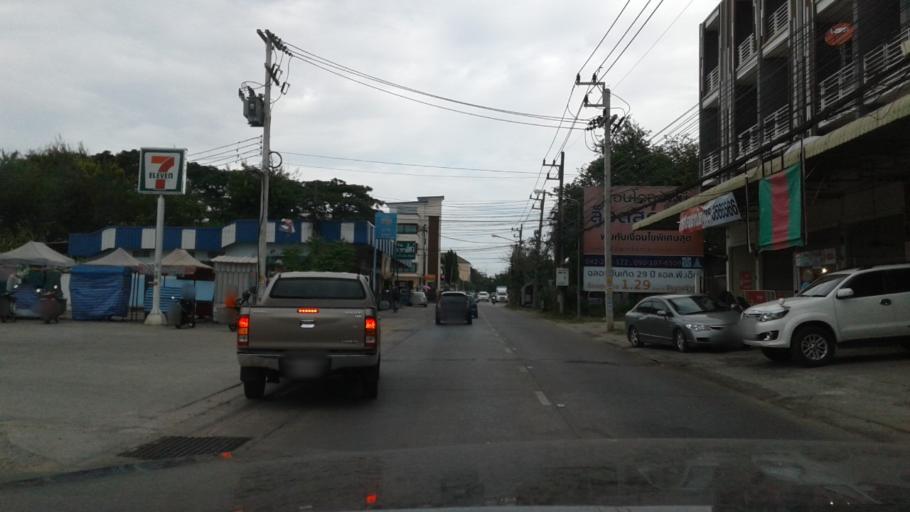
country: TH
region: Changwat Udon Thani
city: Udon Thani
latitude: 17.3994
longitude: 102.7719
